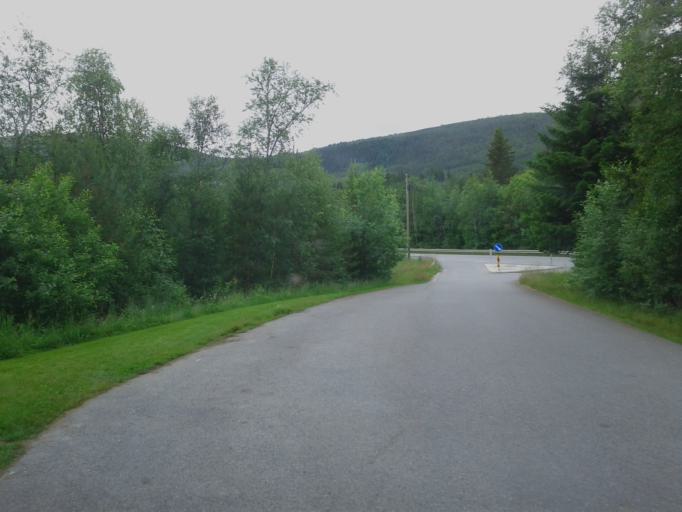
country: NO
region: Sor-Trondelag
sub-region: Holtalen
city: Alen
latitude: 62.8586
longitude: 11.2127
